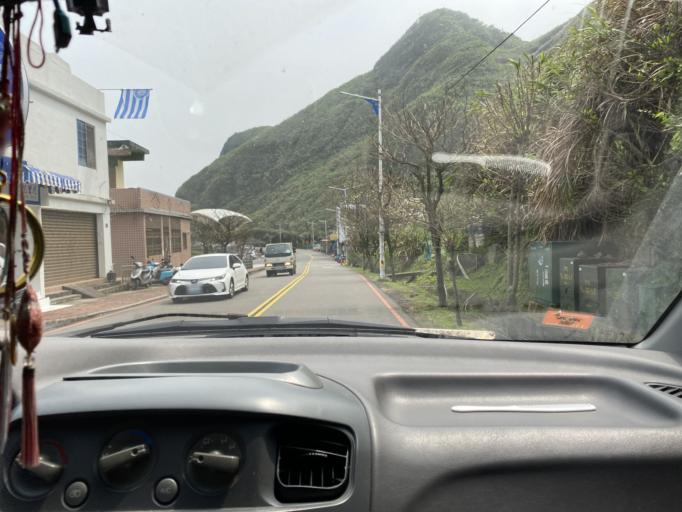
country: TW
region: Taiwan
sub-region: Keelung
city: Keelung
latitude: 25.1641
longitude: 121.7251
